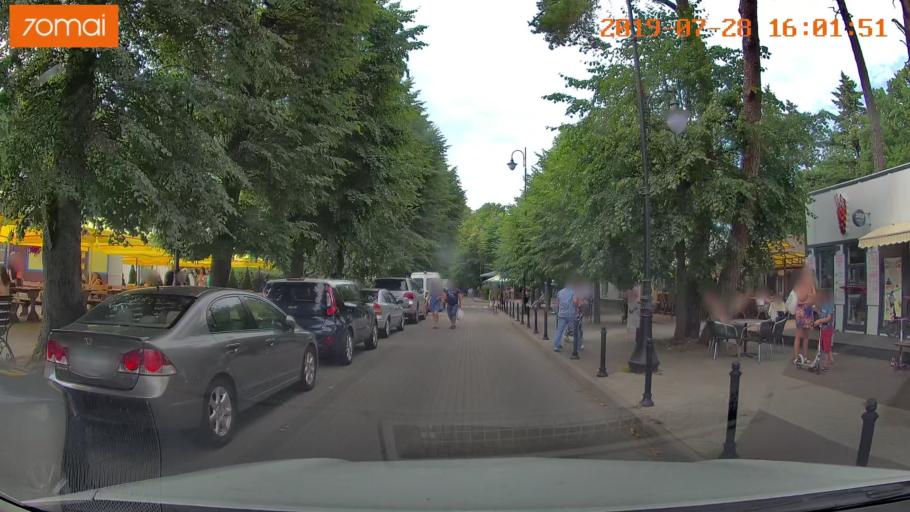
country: RU
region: Kaliningrad
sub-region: Gorod Svetlogorsk
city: Svetlogorsk
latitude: 54.9442
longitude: 20.1530
